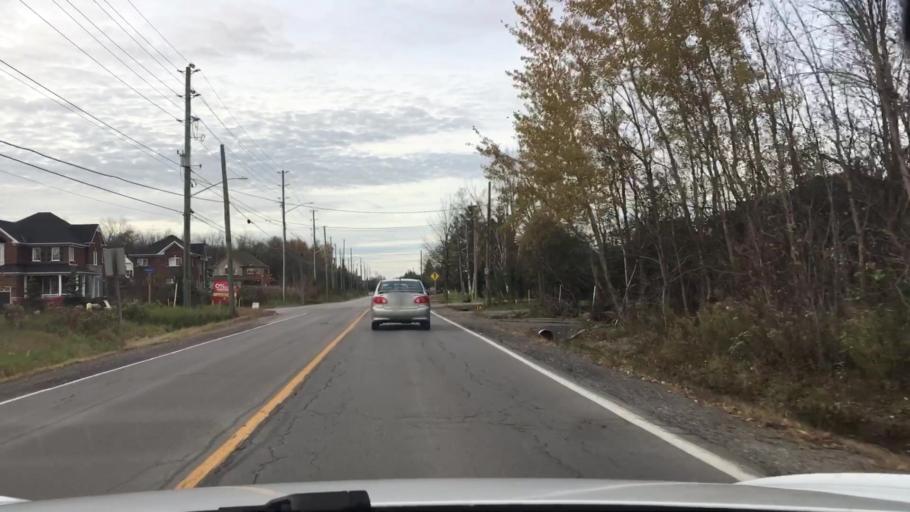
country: CA
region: Ontario
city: Oshawa
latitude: 43.9235
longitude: -78.8208
